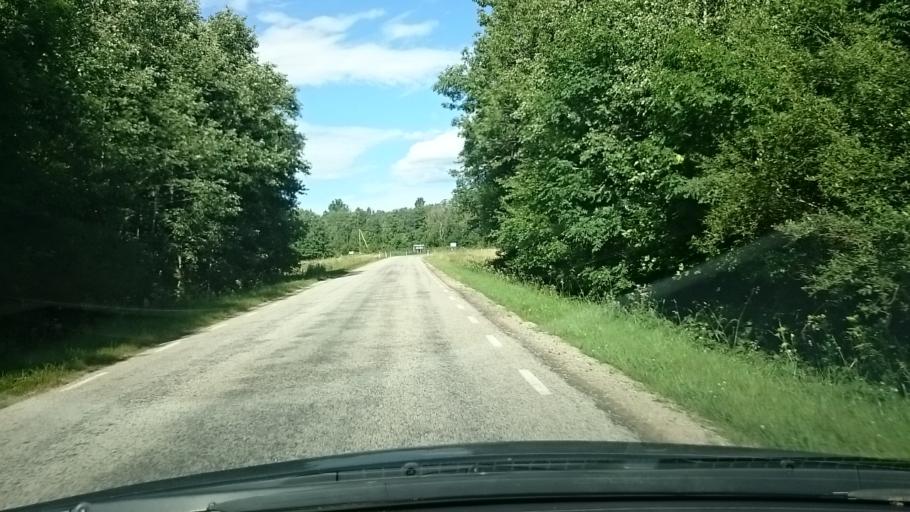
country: EE
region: Laeaene
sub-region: Haapsalu linn
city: Haapsalu
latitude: 59.1263
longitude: 23.5420
